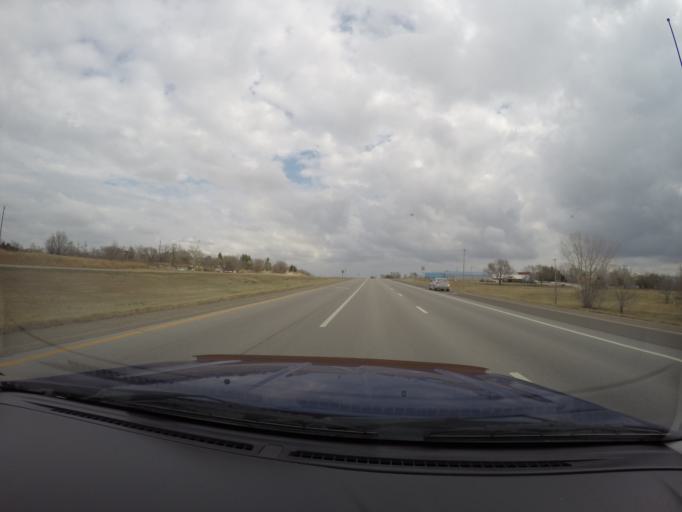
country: US
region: Kansas
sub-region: Riley County
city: Manhattan
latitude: 39.2003
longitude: -96.4414
